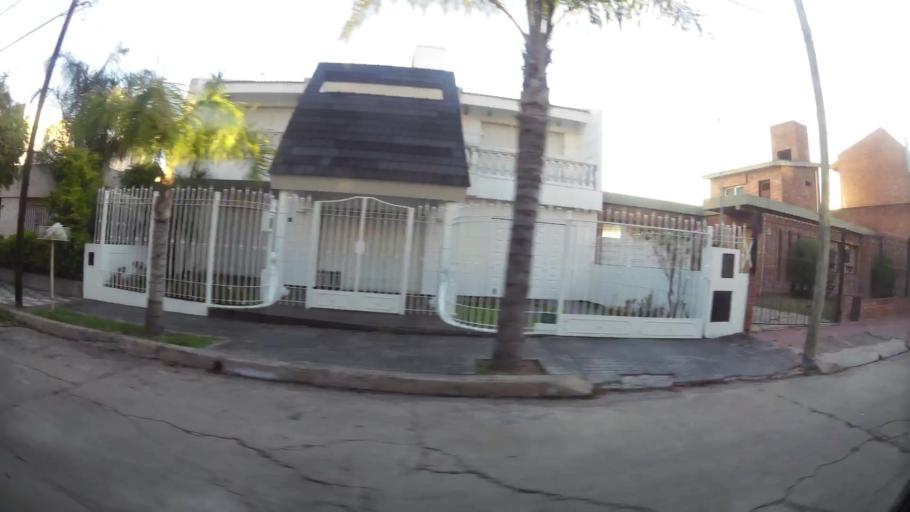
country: AR
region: Cordoba
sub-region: Departamento de Capital
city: Cordoba
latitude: -31.3835
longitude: -64.2106
